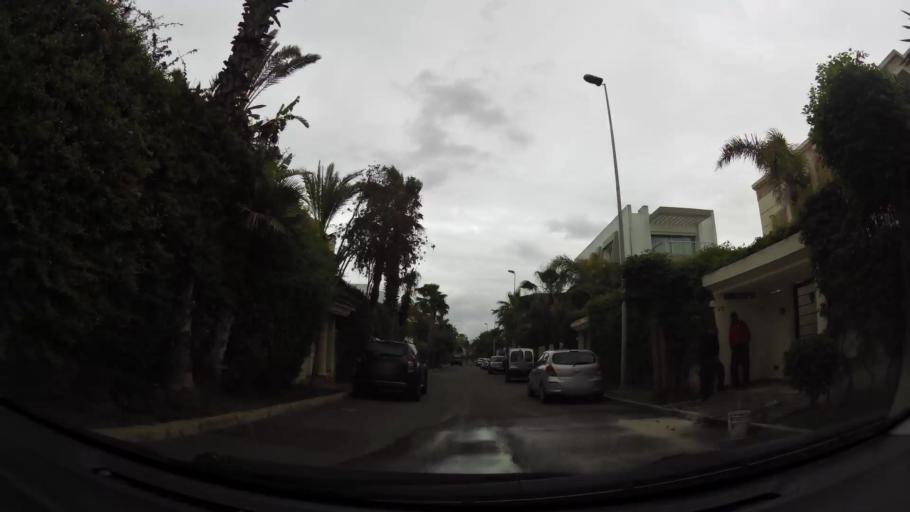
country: MA
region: Grand Casablanca
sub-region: Casablanca
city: Casablanca
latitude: 33.6013
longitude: -7.6584
